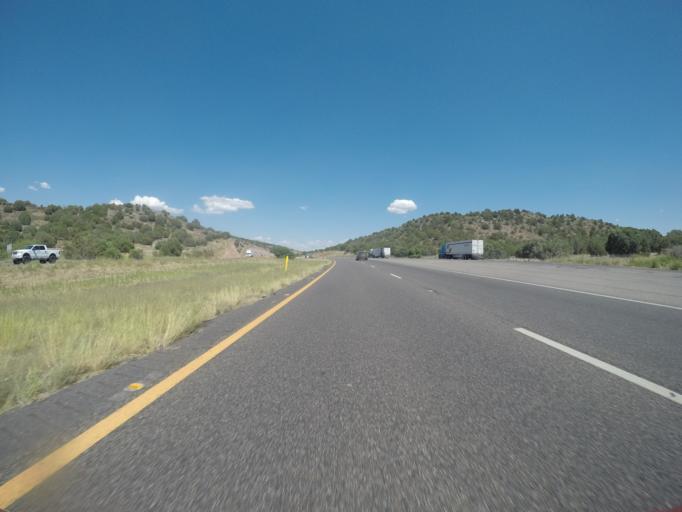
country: US
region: Arizona
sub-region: Yavapai County
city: Camp Verde
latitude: 34.5330
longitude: -111.9671
